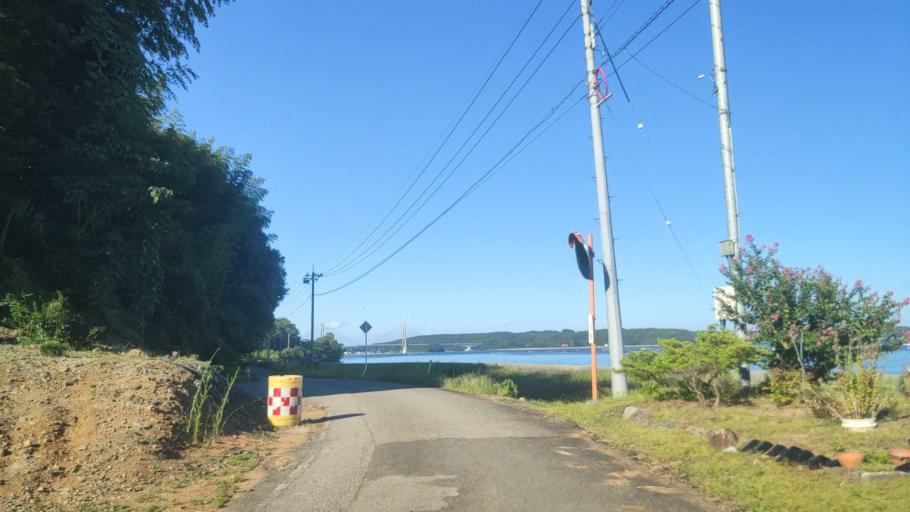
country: JP
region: Ishikawa
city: Nanao
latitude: 37.1213
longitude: 136.8945
